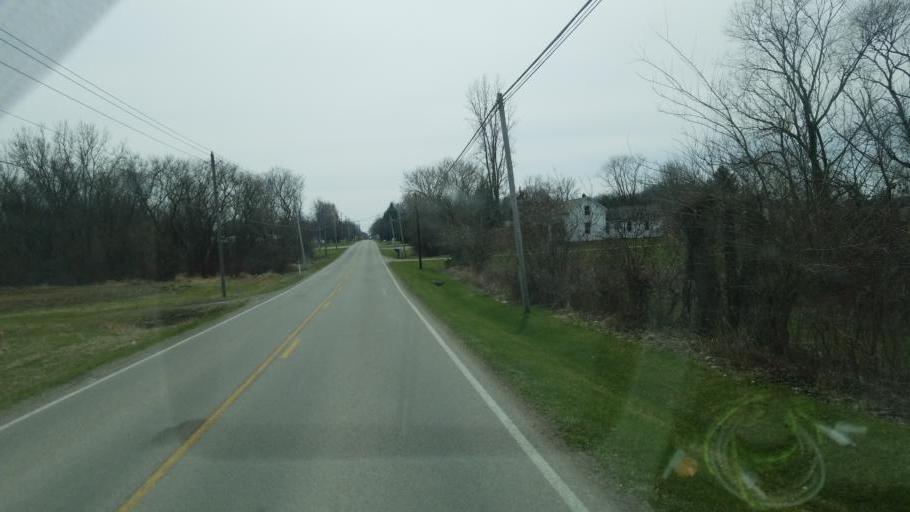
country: US
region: Ohio
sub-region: Huron County
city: Wakeman
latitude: 41.2538
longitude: -82.4916
